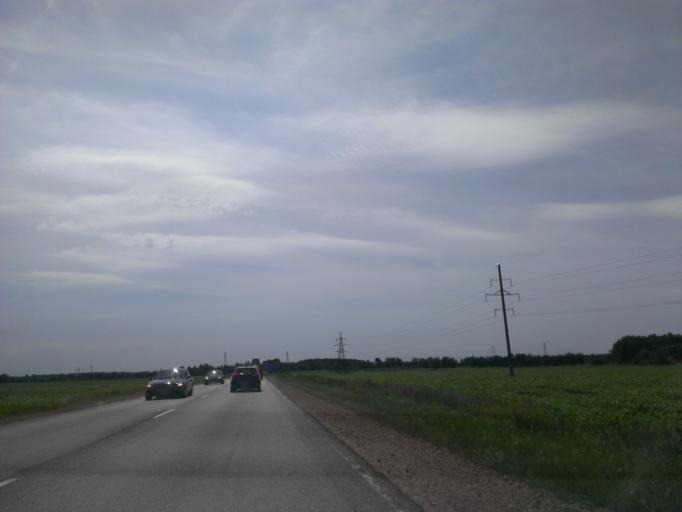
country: LV
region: Salaspils
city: Salaspils
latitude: 56.8604
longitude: 24.4042
